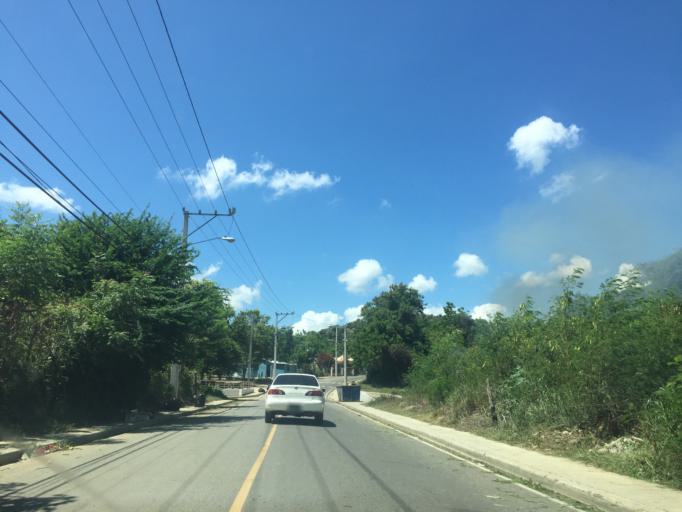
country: DO
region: Santiago
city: Santiago de los Caballeros
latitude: 19.4452
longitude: -70.7427
